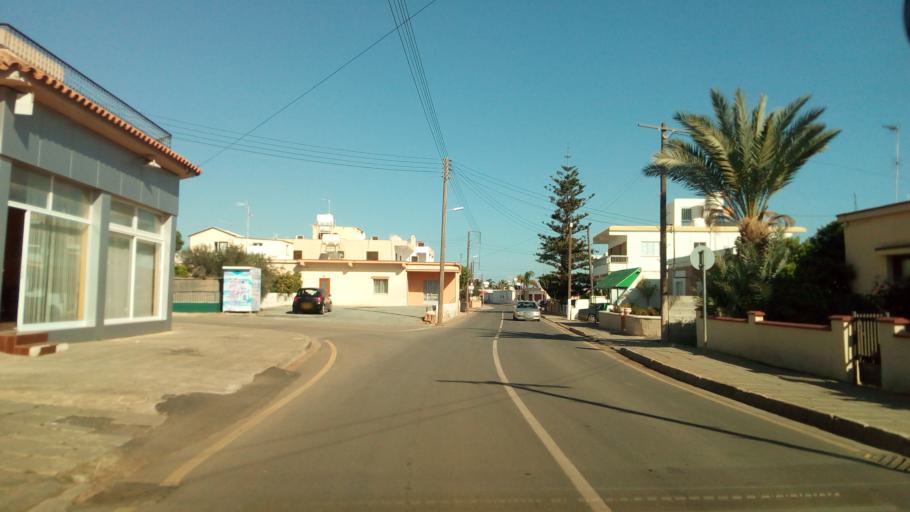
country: CY
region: Ammochostos
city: Liopetri
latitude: 34.9783
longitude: 33.8482
